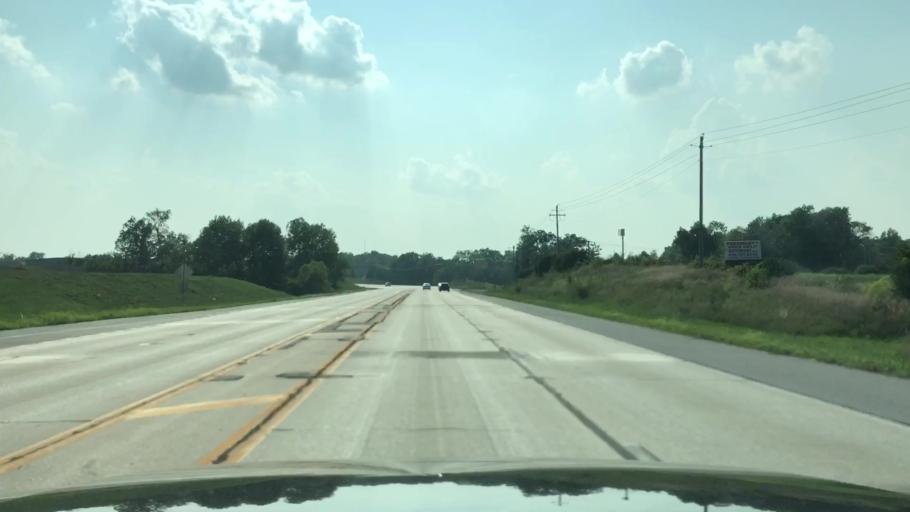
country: US
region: Missouri
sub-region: Saint Charles County
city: Wentzville
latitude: 38.8266
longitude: -90.8410
